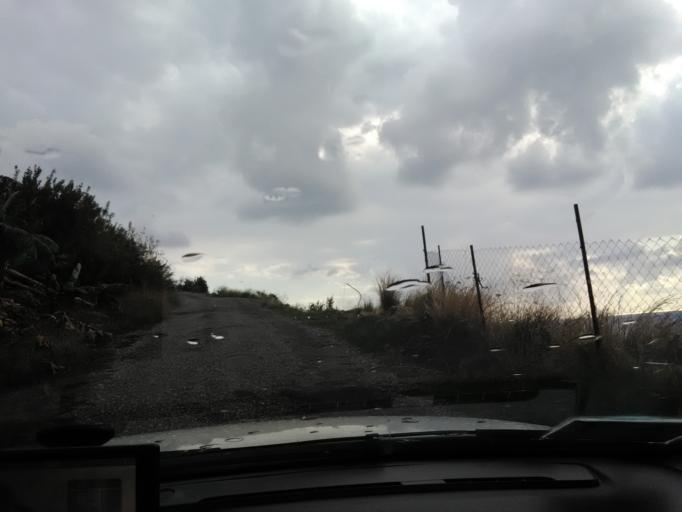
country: TR
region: Antalya
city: Gazipasa
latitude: 36.1571
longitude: 32.4186
